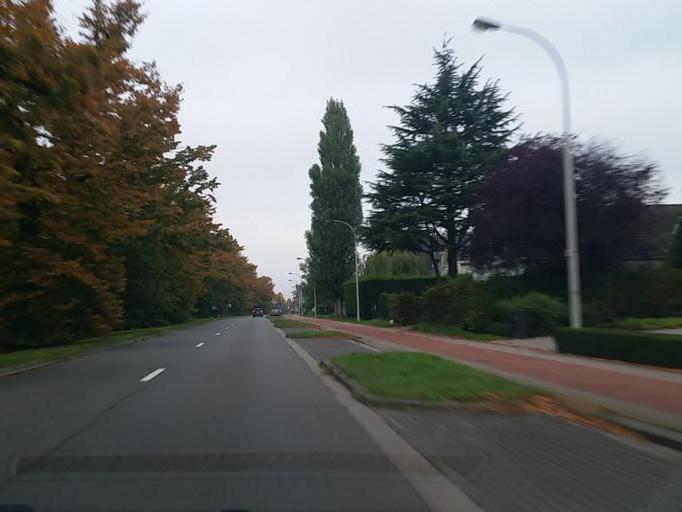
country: BE
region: Flanders
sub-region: Provincie Antwerpen
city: Edegem
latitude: 51.1530
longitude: 4.4336
